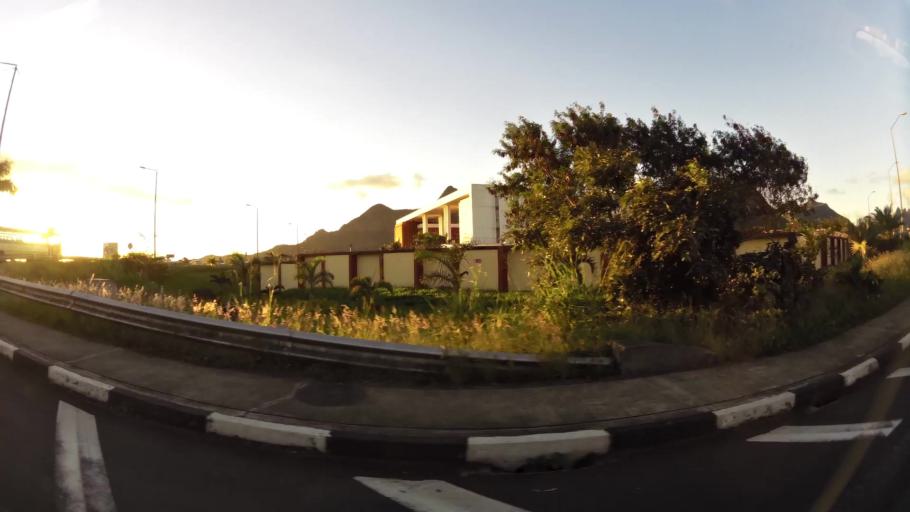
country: MU
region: Moka
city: Moka
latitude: -20.2312
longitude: 57.5018
